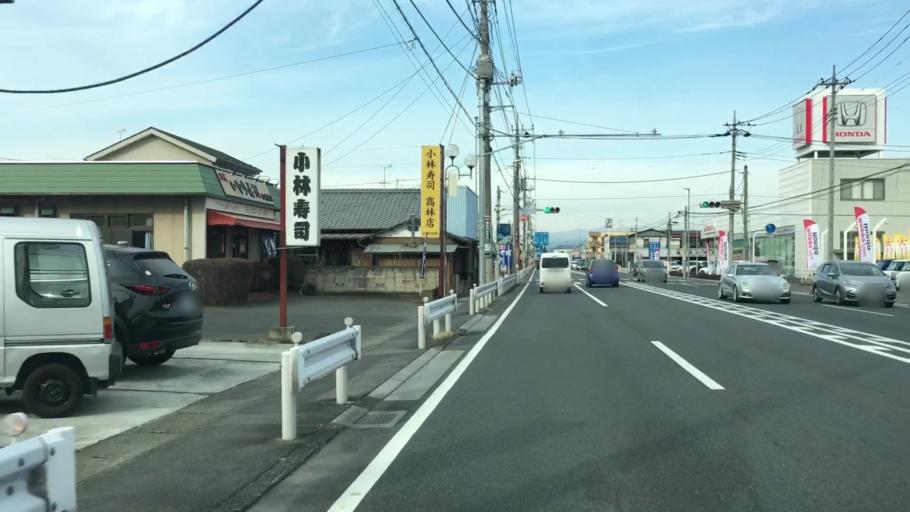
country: JP
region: Saitama
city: Menuma
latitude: 36.2556
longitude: 139.3778
